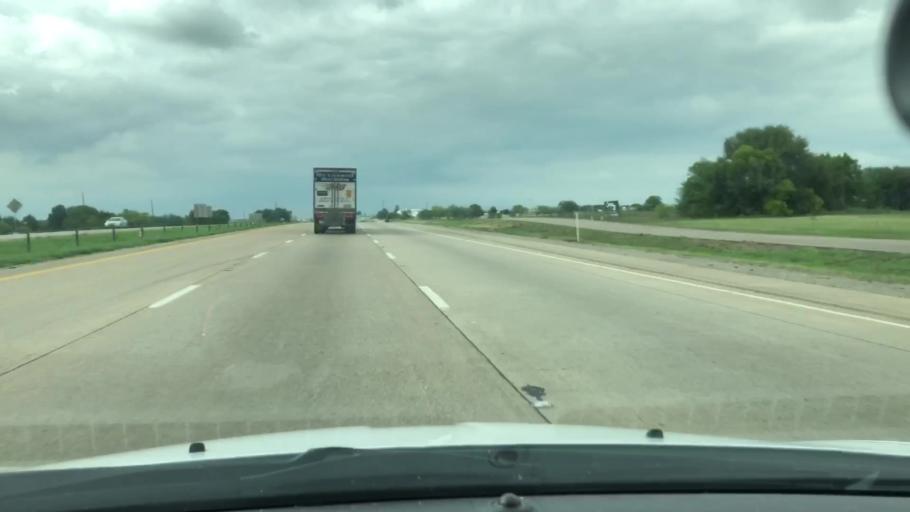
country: US
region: Texas
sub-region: Ellis County
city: Ennis
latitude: 32.3426
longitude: -96.6201
